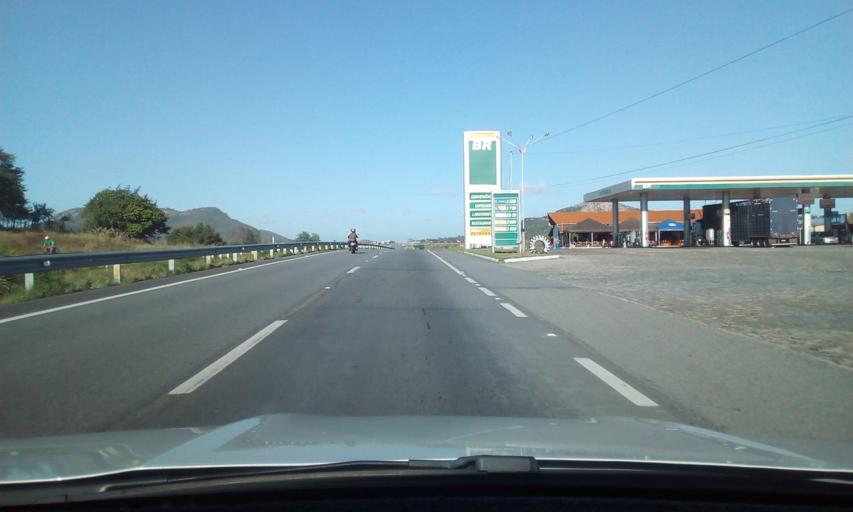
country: BR
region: Paraiba
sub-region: Gurinhem
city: Gurinhem
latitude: -7.1684
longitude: -35.3712
